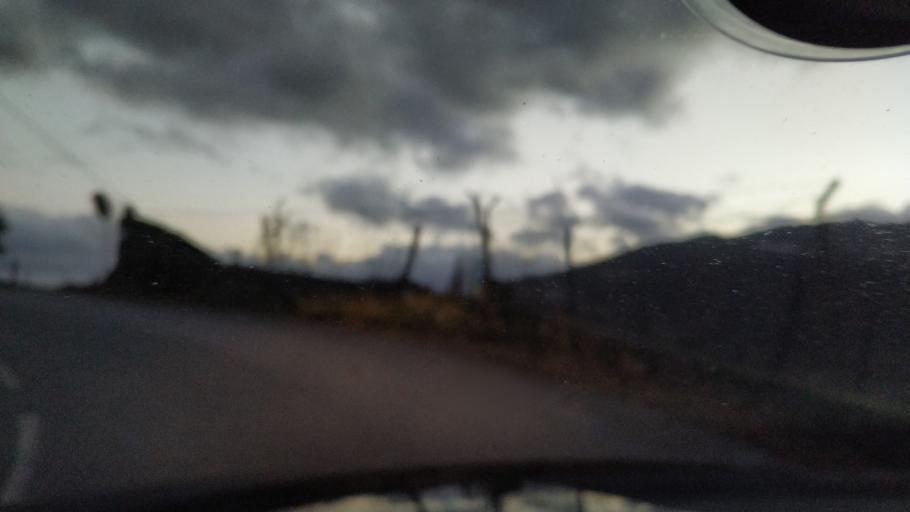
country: PT
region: Vila Real
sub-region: Santa Marta de Penaguiao
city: Santa Marta de Penaguiao
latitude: 41.2368
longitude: -7.7750
